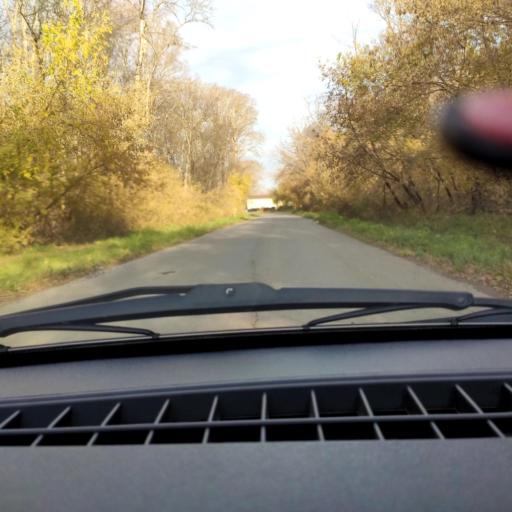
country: RU
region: Bashkortostan
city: Ufa
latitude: 54.7948
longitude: 56.1542
